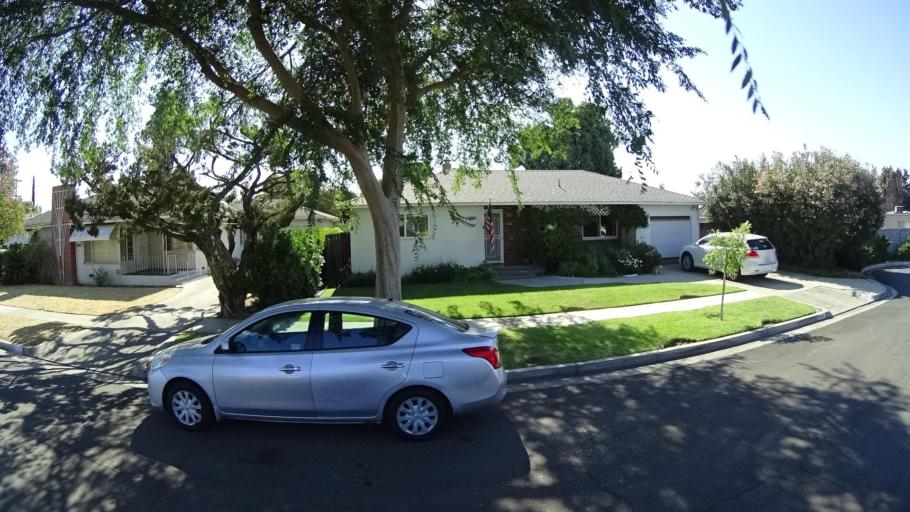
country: US
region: California
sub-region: Fresno County
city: Fresno
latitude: 36.7816
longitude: -119.7655
